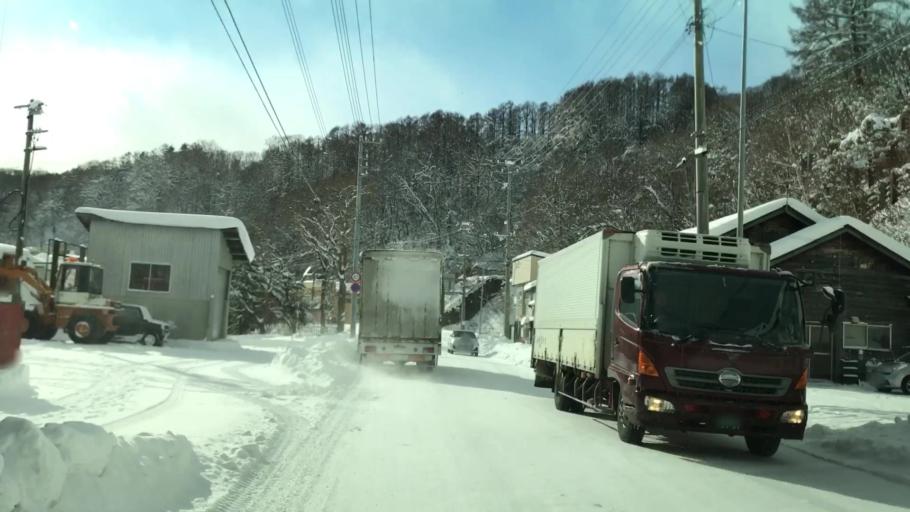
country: JP
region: Hokkaido
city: Yoichi
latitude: 43.2760
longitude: 140.6364
